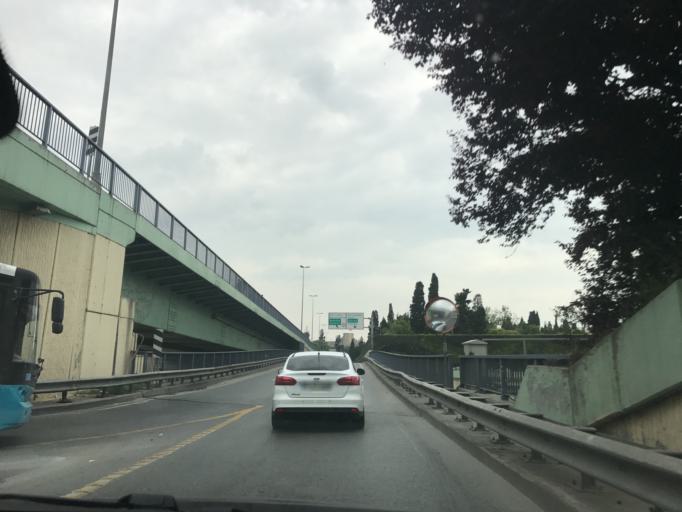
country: TR
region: Istanbul
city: Istanbul
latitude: 41.0337
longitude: 28.9290
